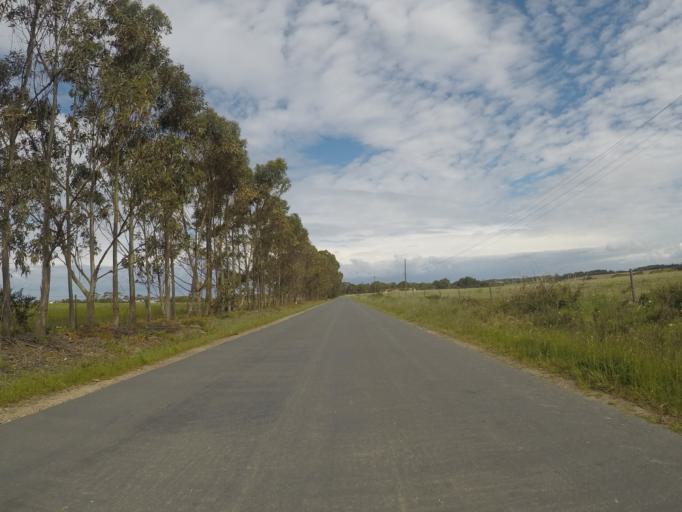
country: PT
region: Beja
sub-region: Odemira
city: Sao Teotonio
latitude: 37.4920
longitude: -8.7823
